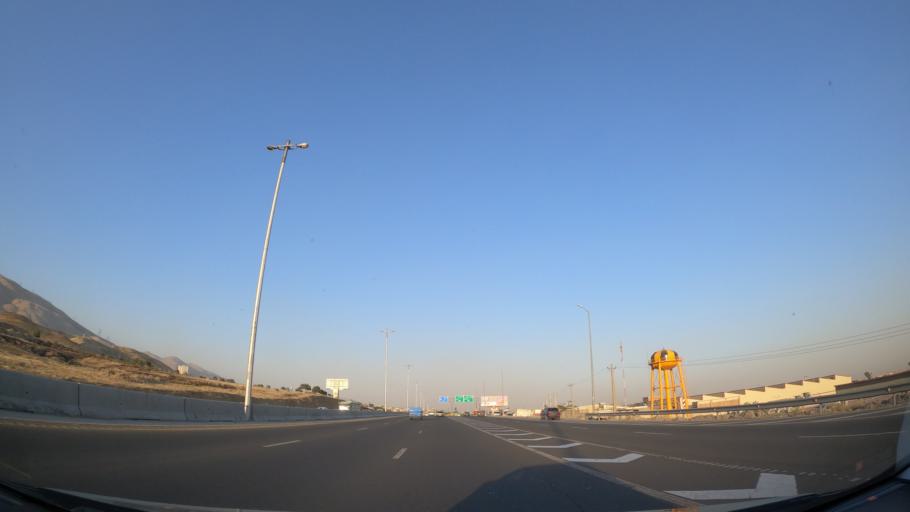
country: IR
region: Tehran
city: Shahr-e Qods
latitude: 35.7425
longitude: 51.1092
